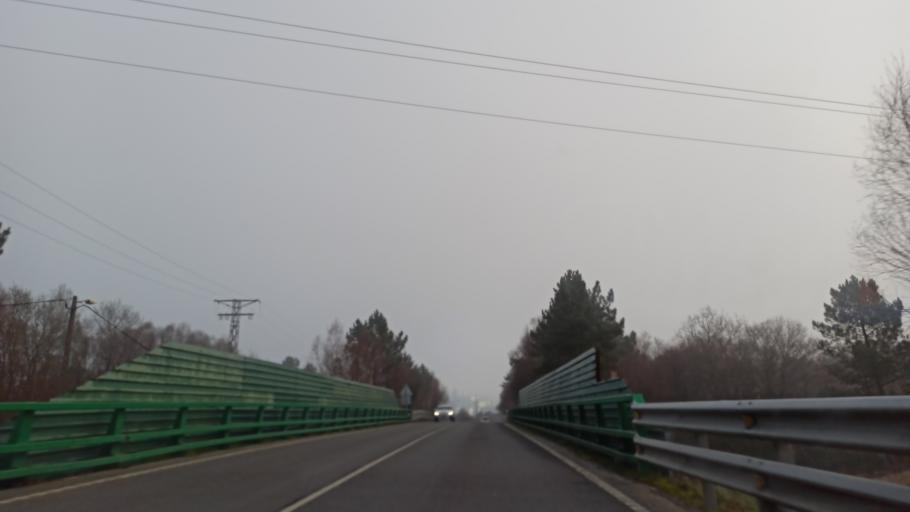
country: ES
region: Galicia
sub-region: Provincia da Coruna
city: As Pontes de Garcia Rodriguez
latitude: 43.4387
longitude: -7.8779
